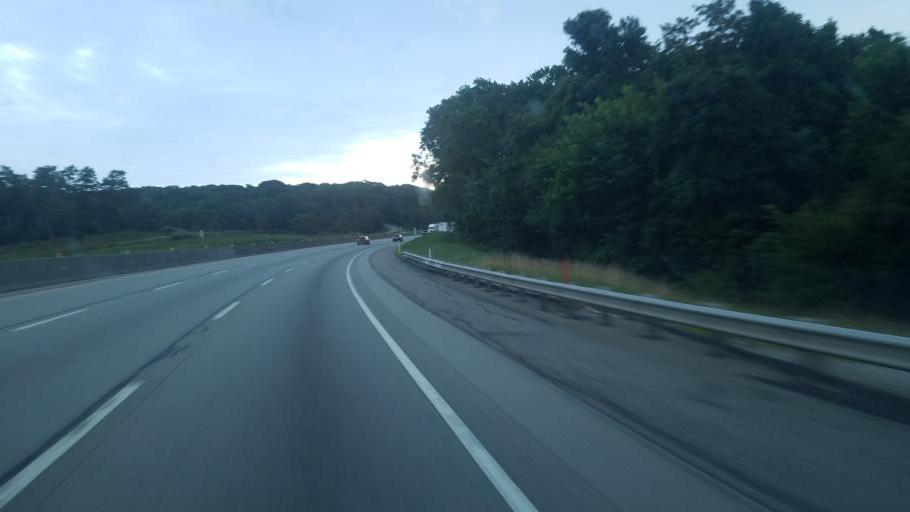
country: US
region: Pennsylvania
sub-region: Westmoreland County
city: Ligonier
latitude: 40.1245
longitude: -79.2819
